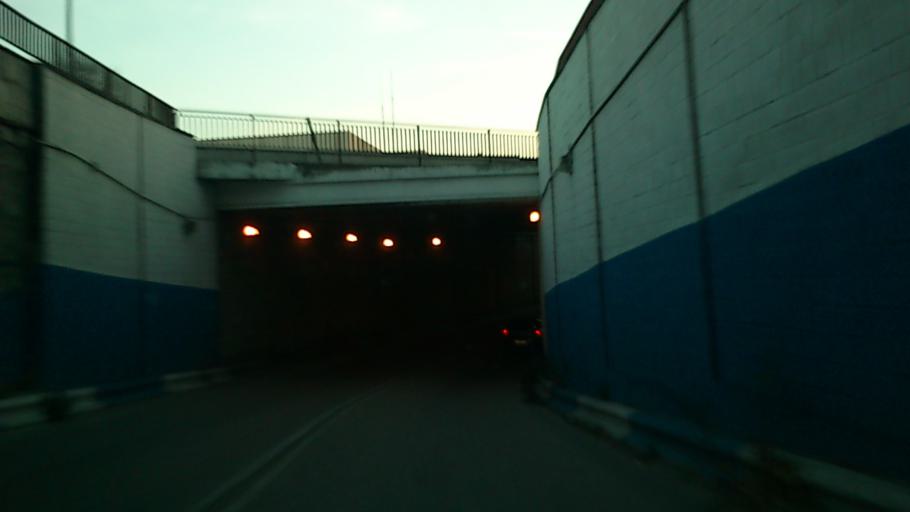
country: ES
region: Madrid
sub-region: Provincia de Madrid
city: San Fernando de Henares
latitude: 40.4429
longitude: -3.5413
